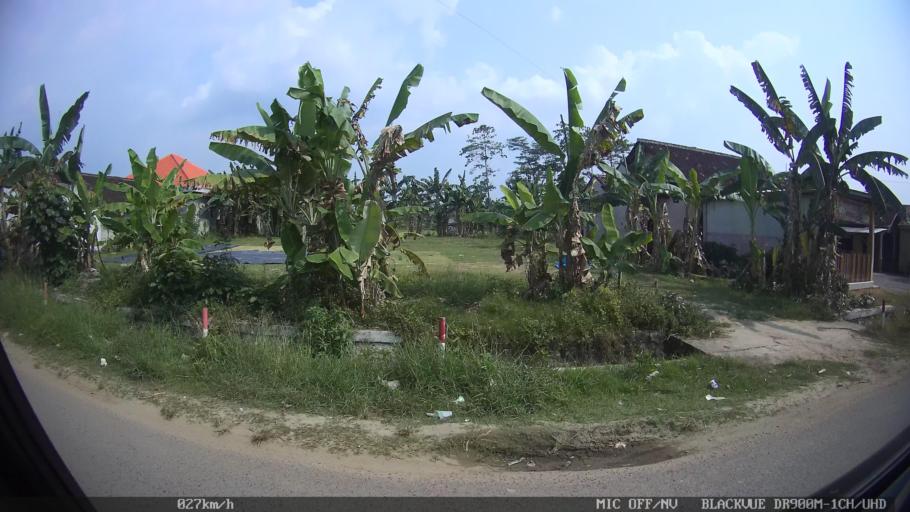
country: ID
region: Lampung
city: Kedondong
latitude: -5.4104
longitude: 104.9949
